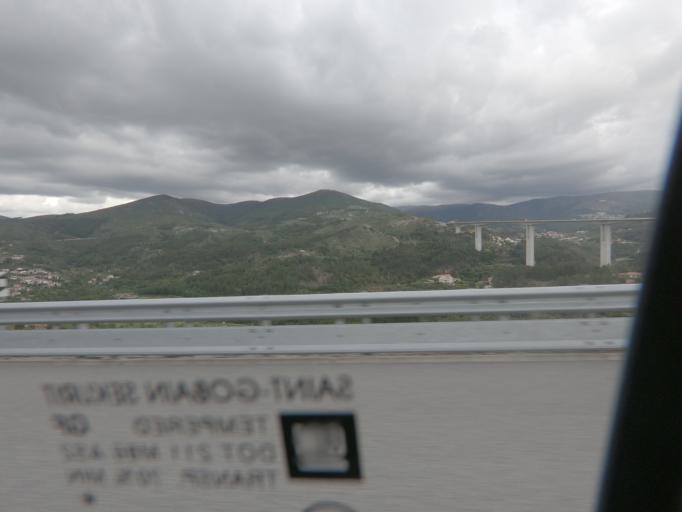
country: PT
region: Porto
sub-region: Amarante
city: Amarante
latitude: 41.2529
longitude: -7.9953
